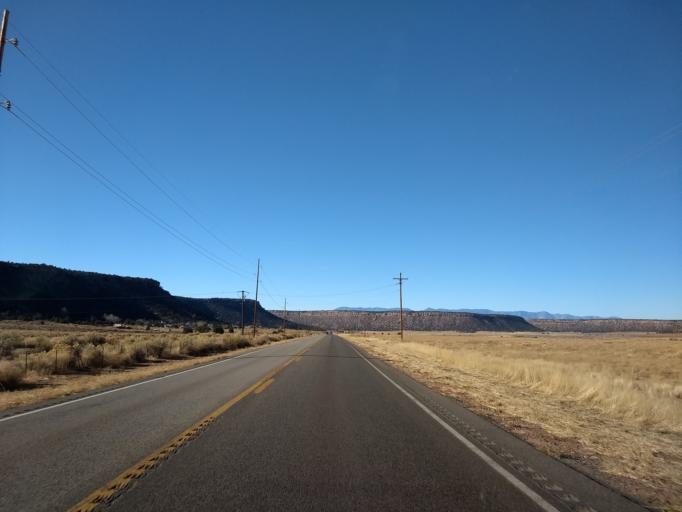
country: US
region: Utah
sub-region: Washington County
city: LaVerkin
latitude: 37.1036
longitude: -113.1340
